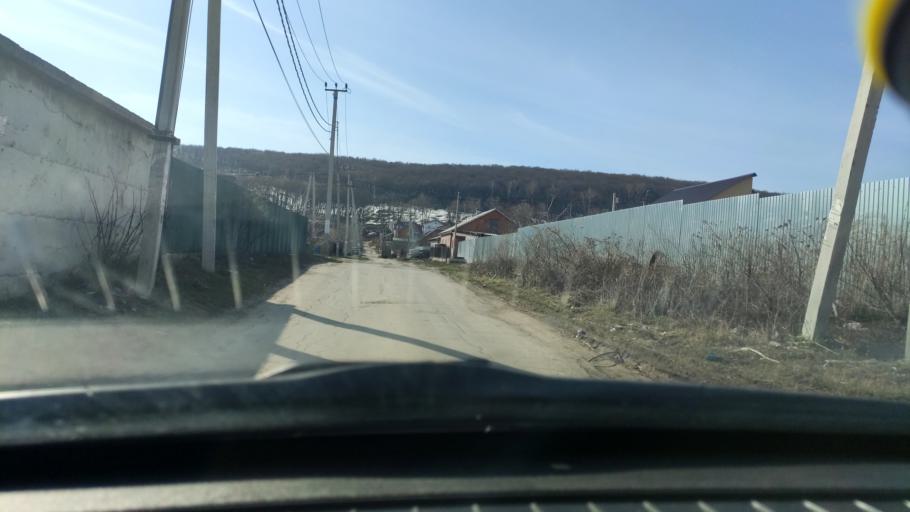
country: RU
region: Samara
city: Zhigulevsk
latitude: 53.3929
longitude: 49.4927
